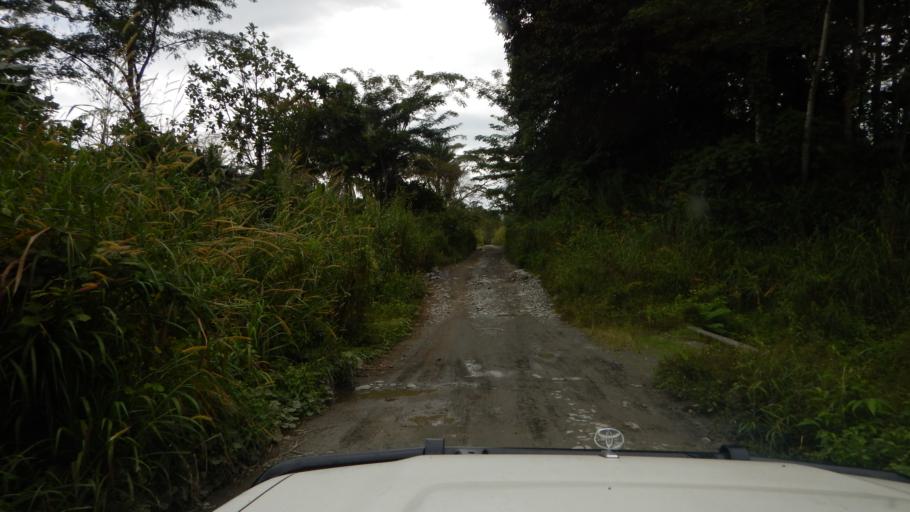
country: PG
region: Northern Province
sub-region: Sohe
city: Kokoda
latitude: -8.9157
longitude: 147.8749
